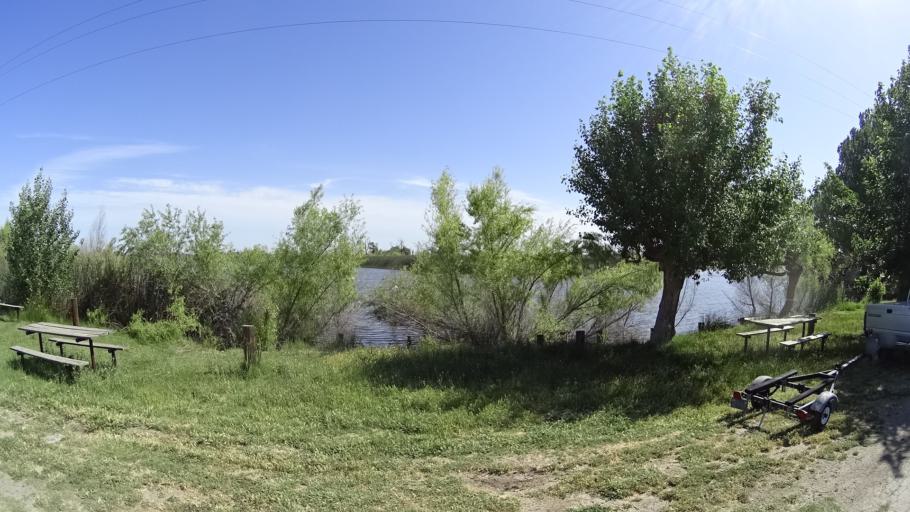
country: US
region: California
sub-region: Kings County
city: Lemoore Station
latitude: 36.2493
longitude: -119.8558
